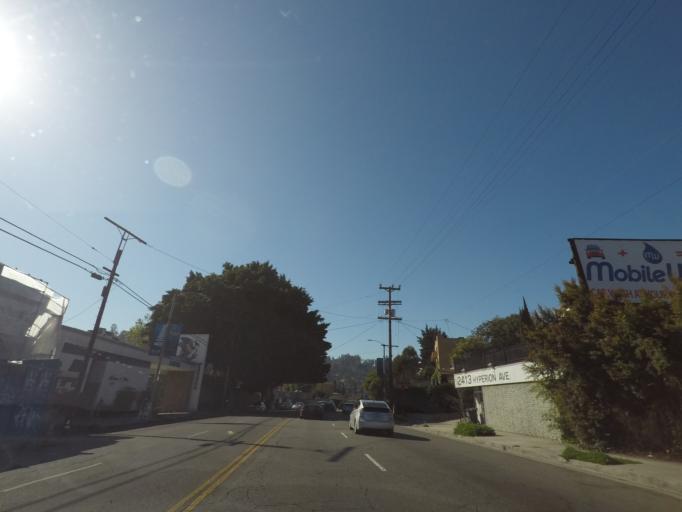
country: US
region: California
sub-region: Los Angeles County
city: Silver Lake
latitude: 34.1032
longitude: -118.2732
